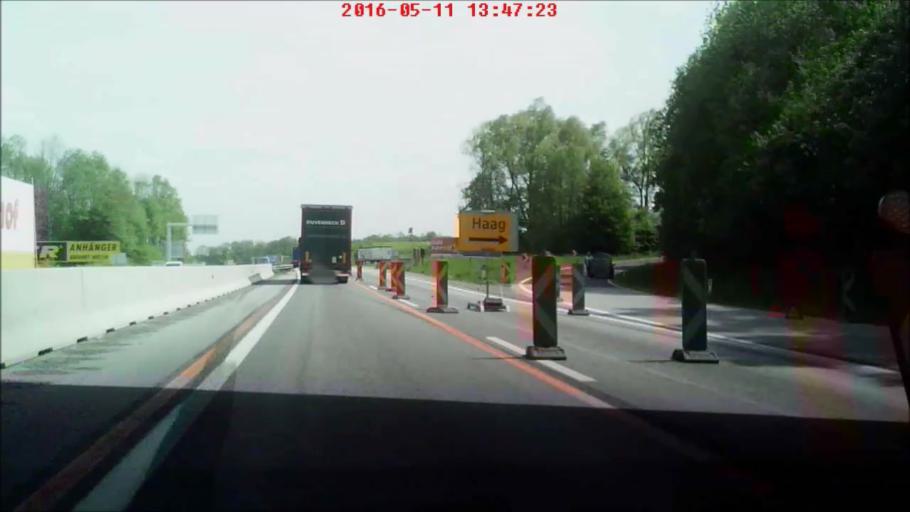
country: AT
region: Upper Austria
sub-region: Politischer Bezirk Vocklabruck
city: Wolfsegg am Hausruck
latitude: 48.2004
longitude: 13.6404
